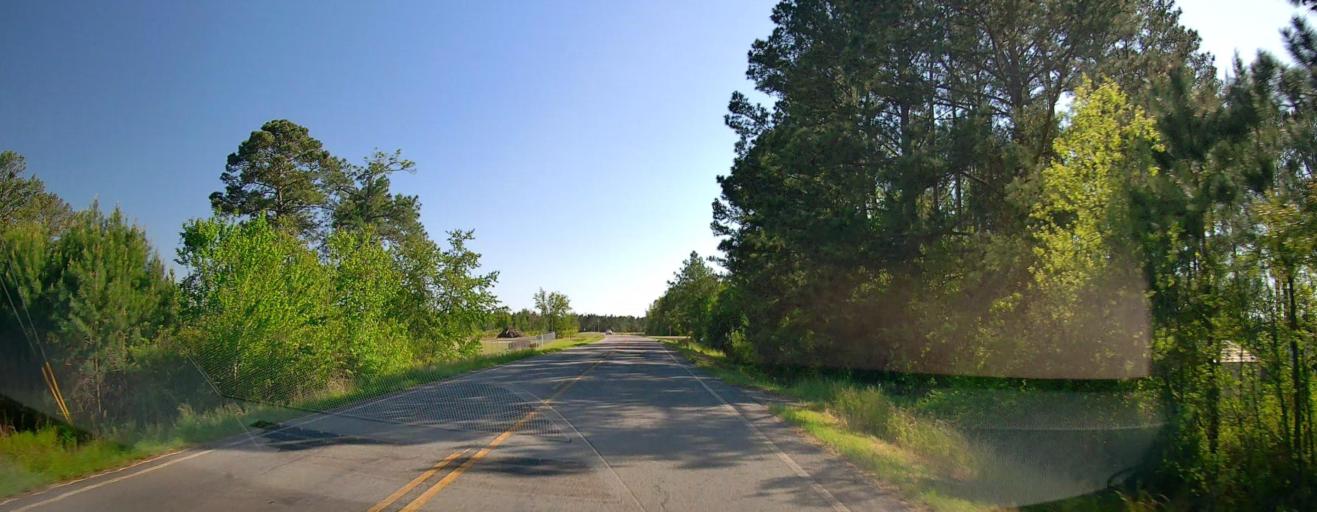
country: US
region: Georgia
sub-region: Wilcox County
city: Rochelle
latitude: 32.1019
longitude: -83.5022
